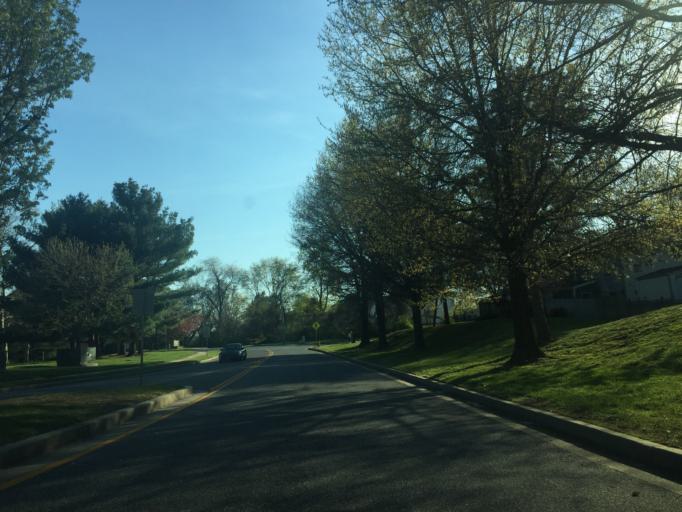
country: US
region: Maryland
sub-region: Harford County
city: Riverside
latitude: 39.4755
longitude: -76.2393
